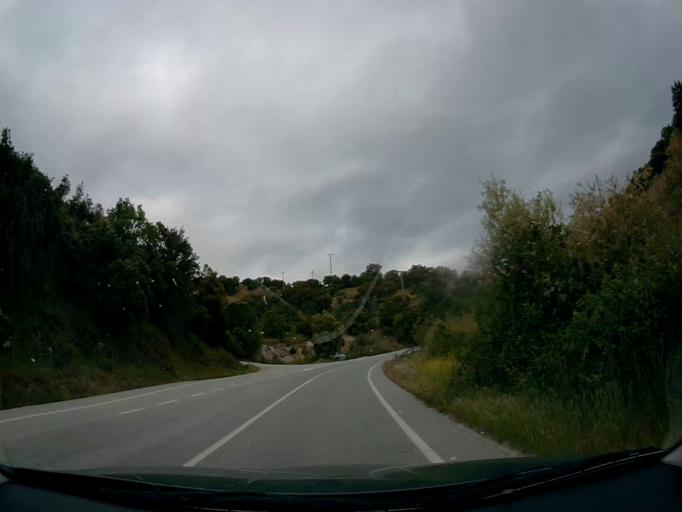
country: ES
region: Madrid
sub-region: Provincia de Madrid
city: Navalagamella
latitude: 40.4420
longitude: -4.1152
